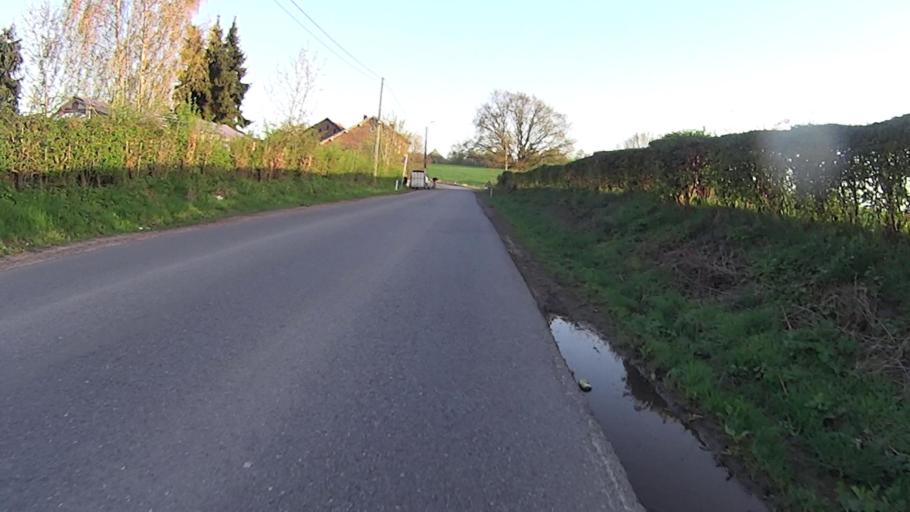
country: BE
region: Flanders
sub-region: Provincie Limburg
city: Sint-Pieters-Voeren
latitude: 50.7259
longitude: 5.7908
